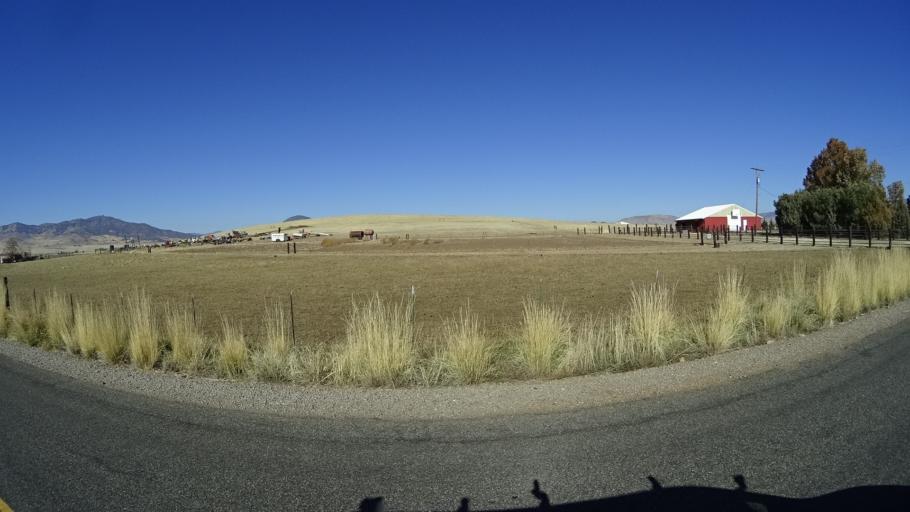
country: US
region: California
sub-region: Siskiyou County
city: Montague
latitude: 41.7558
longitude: -122.4644
